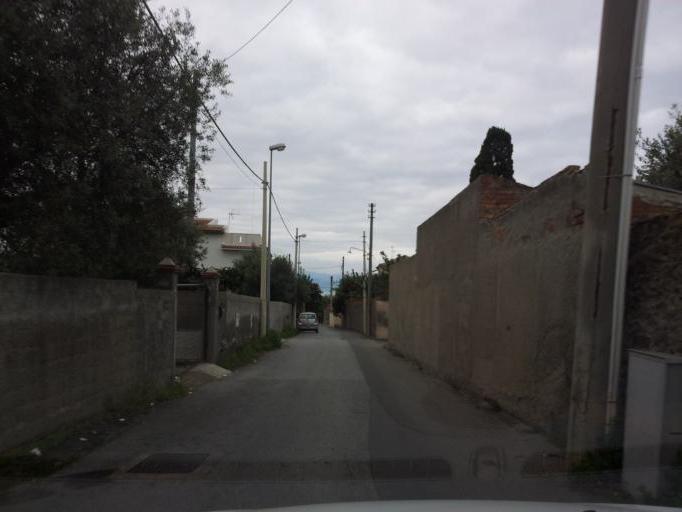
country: IT
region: Sicily
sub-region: Messina
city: Milazzo
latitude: 38.2489
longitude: 15.2454
